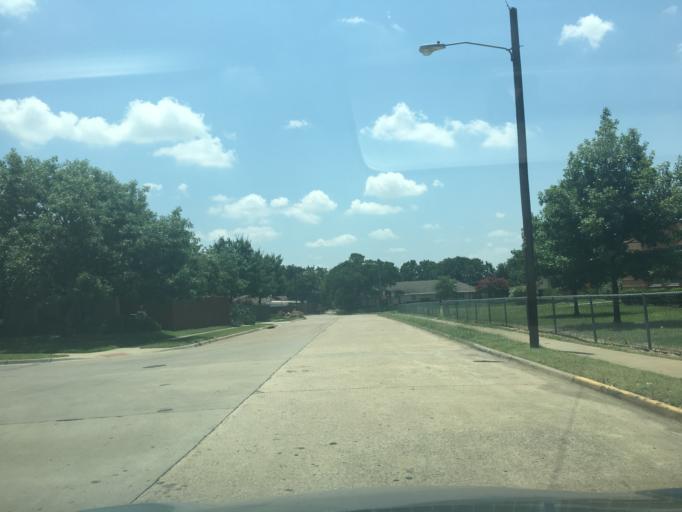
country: US
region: Texas
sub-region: Dallas County
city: Addison
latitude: 32.9171
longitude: -96.8438
